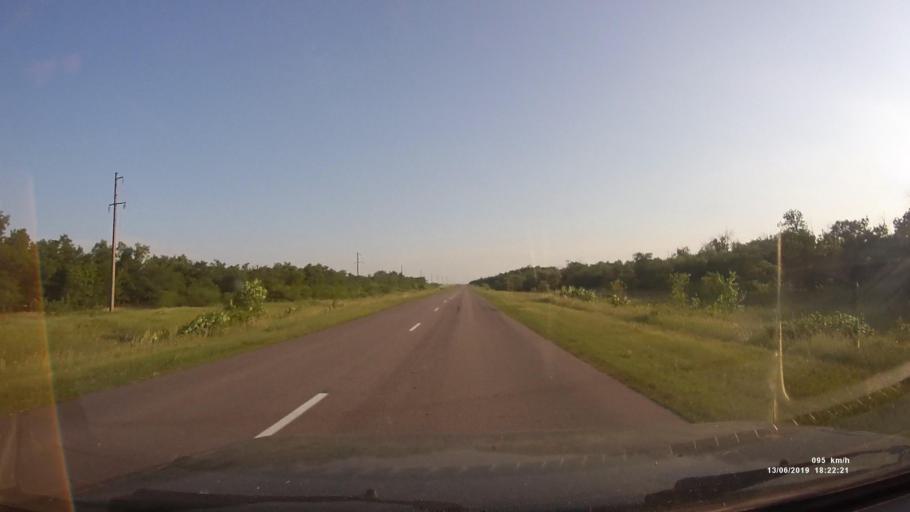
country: RU
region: Rostov
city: Kazanskaya
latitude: 49.8596
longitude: 41.2794
